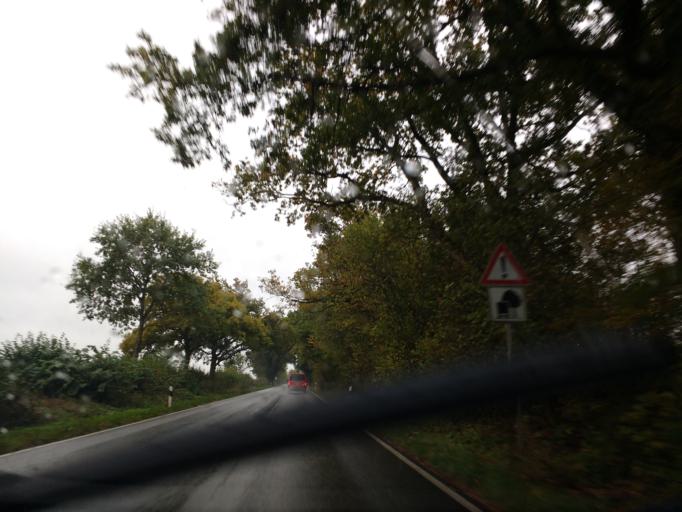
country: DE
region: Schleswig-Holstein
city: Eutin
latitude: 54.1127
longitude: 10.6583
